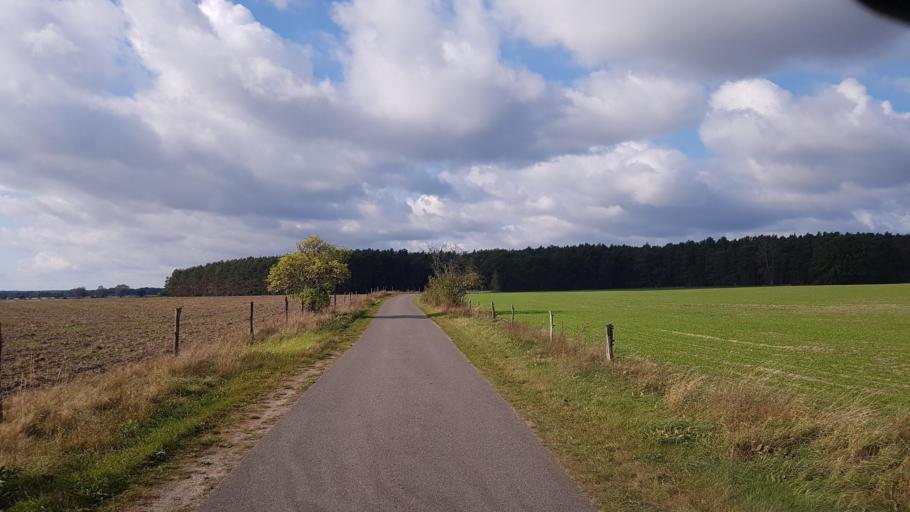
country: DE
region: Brandenburg
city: Vetschau
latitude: 51.7153
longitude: 14.0796
